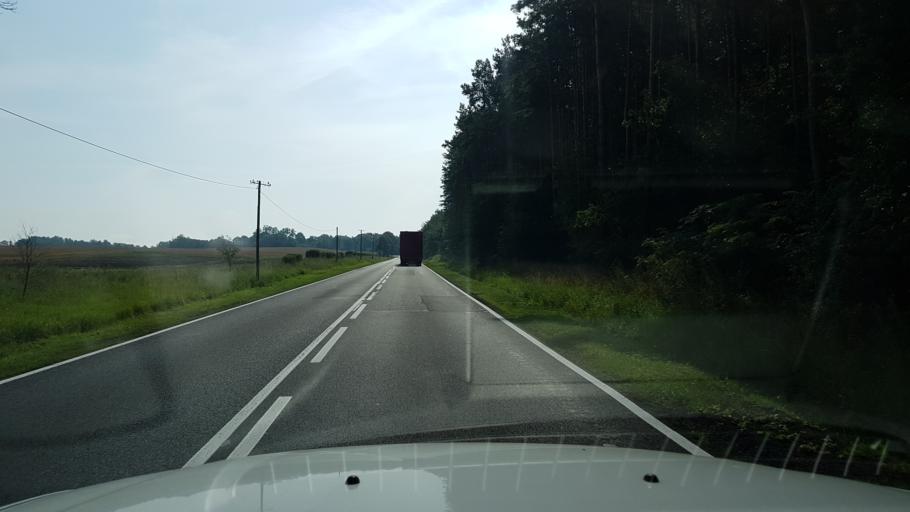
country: PL
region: West Pomeranian Voivodeship
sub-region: Powiat drawski
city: Kalisz Pomorski
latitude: 53.2980
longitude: 15.8238
